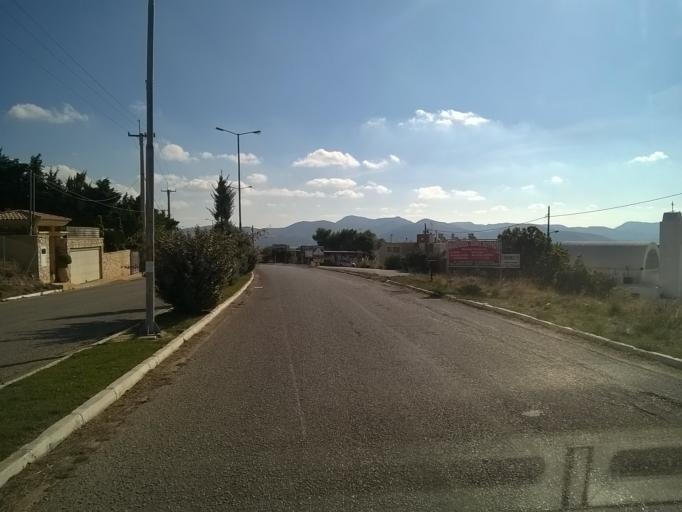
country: GR
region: Attica
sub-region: Nomarchia Anatolikis Attikis
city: Saronida
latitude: 37.7418
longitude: 23.9242
